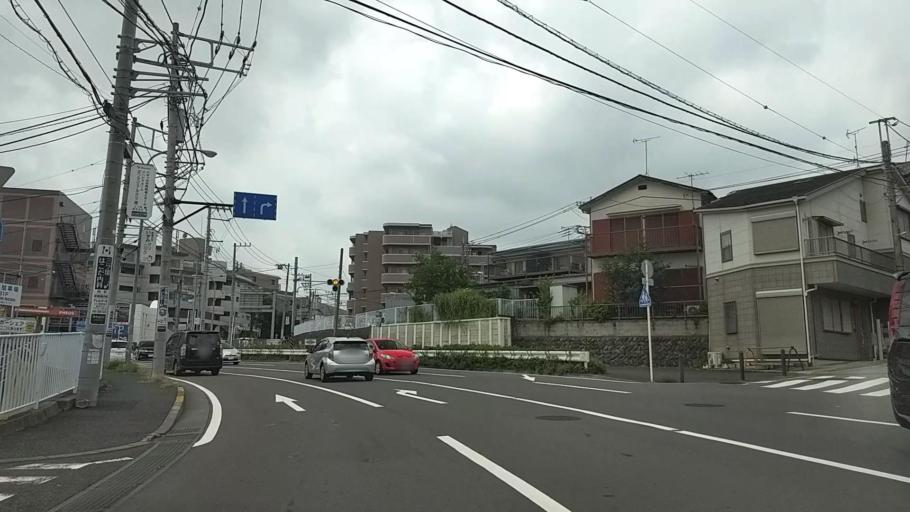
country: JP
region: Kanagawa
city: Minami-rinkan
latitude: 35.4674
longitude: 139.5067
